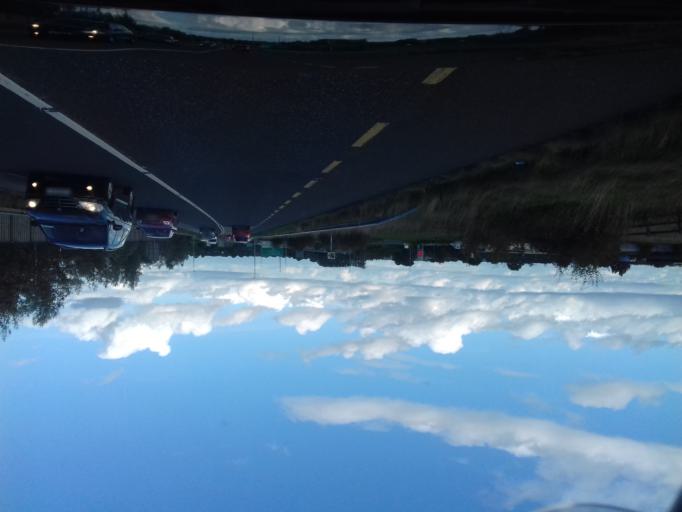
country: IE
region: Leinster
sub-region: Uibh Fhaili
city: Tullamore
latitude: 53.2645
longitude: -7.4639
